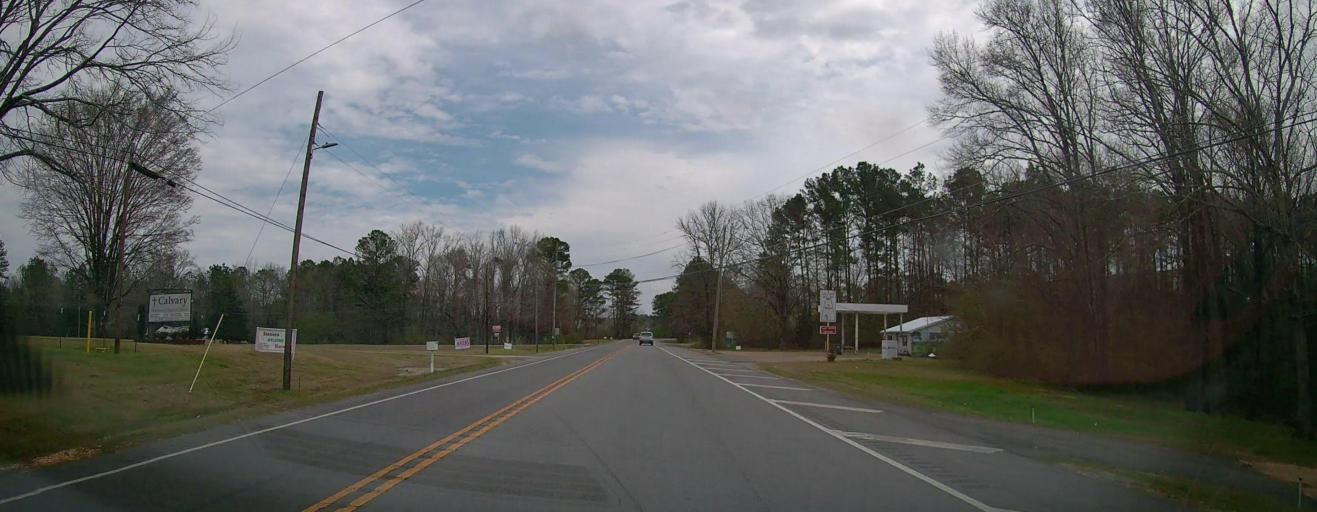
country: US
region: Alabama
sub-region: Marion County
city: Guin
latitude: 33.9869
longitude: -87.9216
